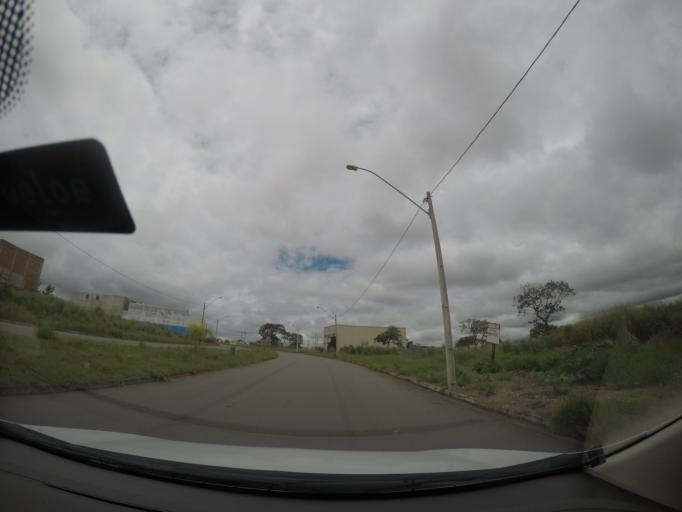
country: BR
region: Goias
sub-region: Goiania
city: Goiania
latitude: -16.7466
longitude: -49.3369
